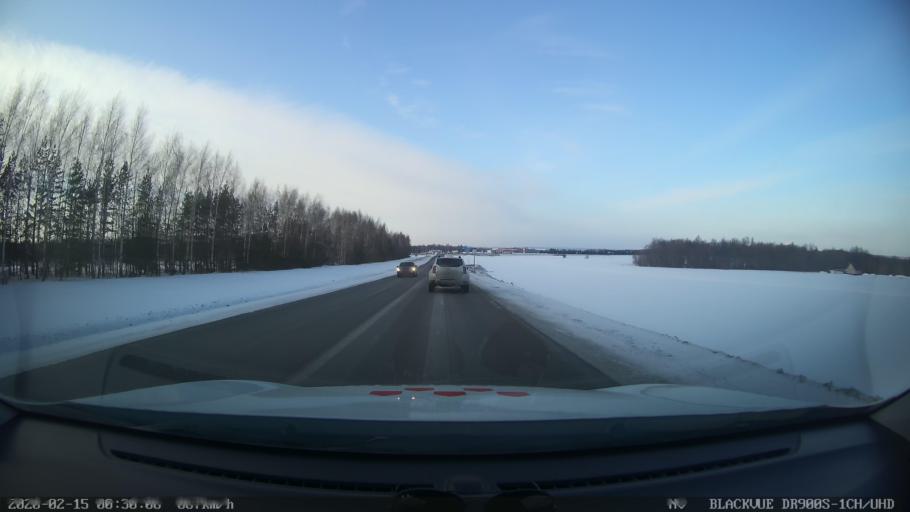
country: RU
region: Tatarstan
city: Verkhniy Uslon
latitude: 55.6565
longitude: 48.8610
